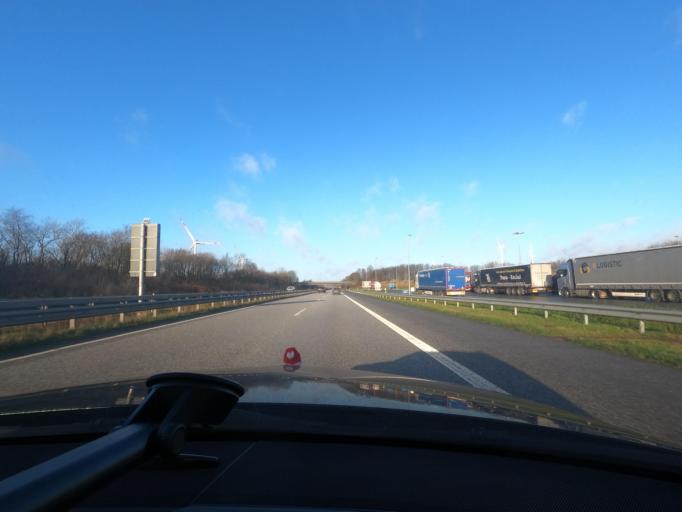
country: DE
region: Schleswig-Holstein
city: Bollingstedt
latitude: 54.6354
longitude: 9.4393
